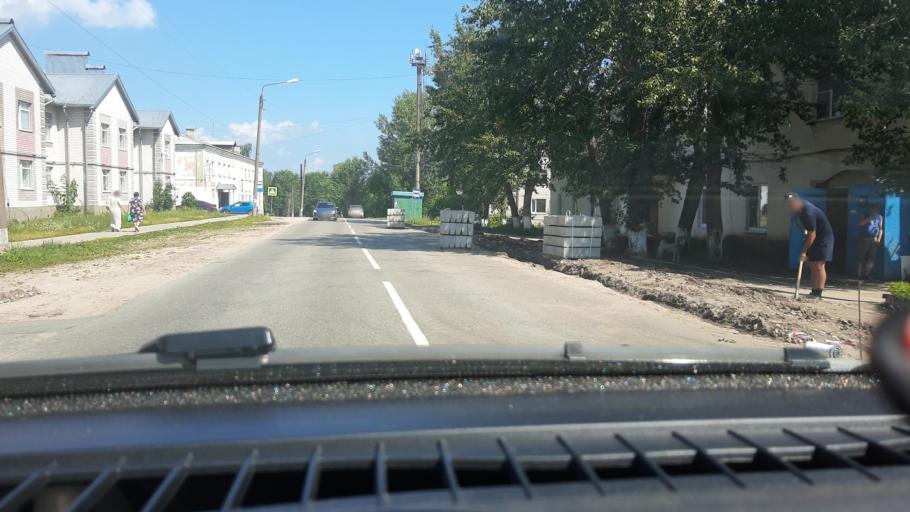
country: RU
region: Nizjnij Novgorod
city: Afonino
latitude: 56.2891
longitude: 44.1912
